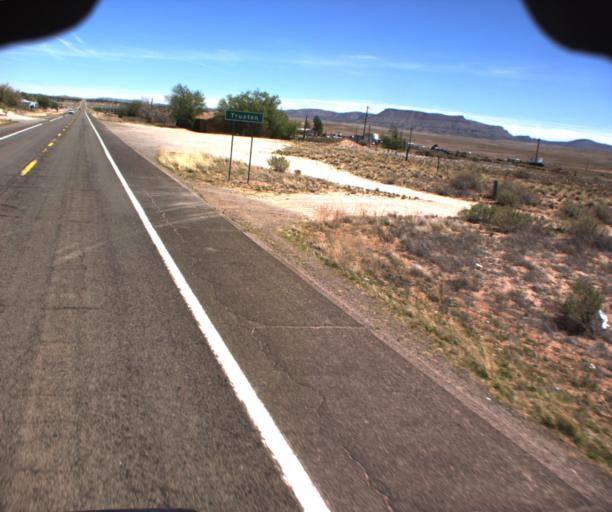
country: US
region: Arizona
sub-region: Mohave County
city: Peach Springs
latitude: 35.4826
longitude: -113.5680
